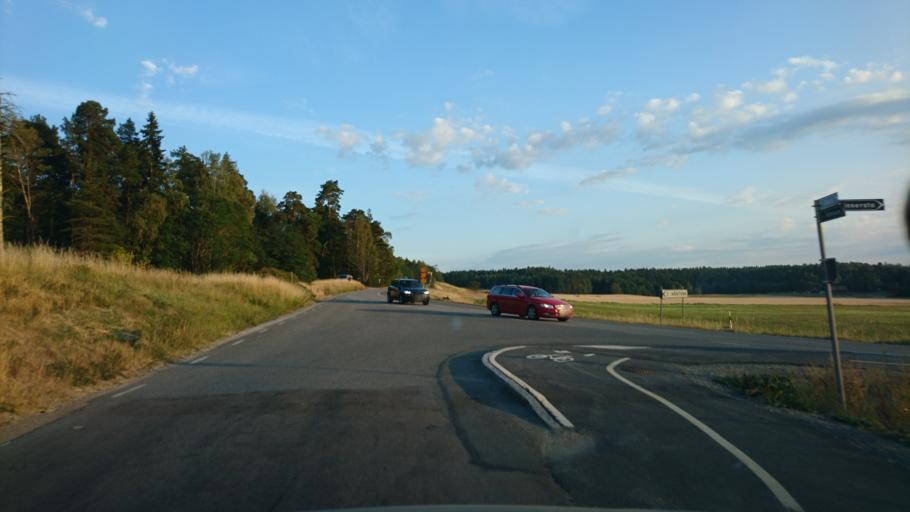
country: SE
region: Uppsala
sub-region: Uppsala Kommun
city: Saevja
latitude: 59.7866
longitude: 17.6652
